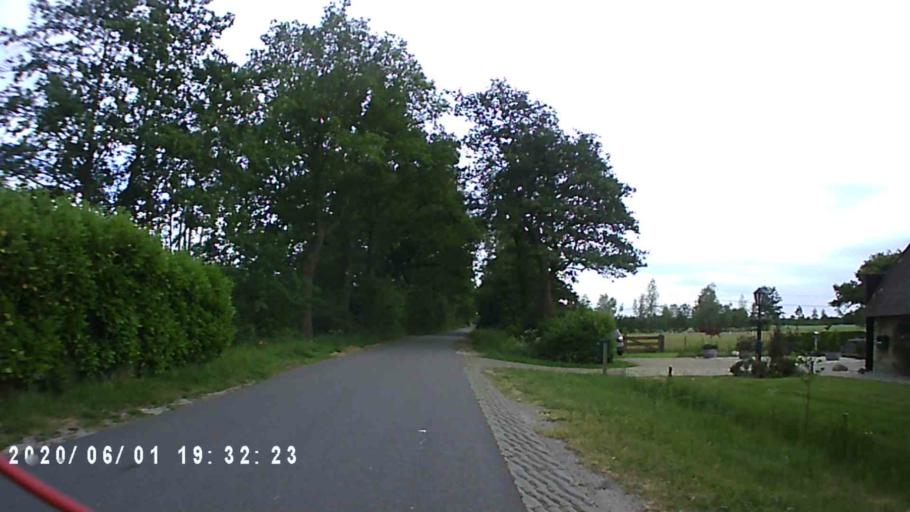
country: NL
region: Friesland
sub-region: Gemeente Achtkarspelen
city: Augustinusga
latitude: 53.2119
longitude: 6.1575
